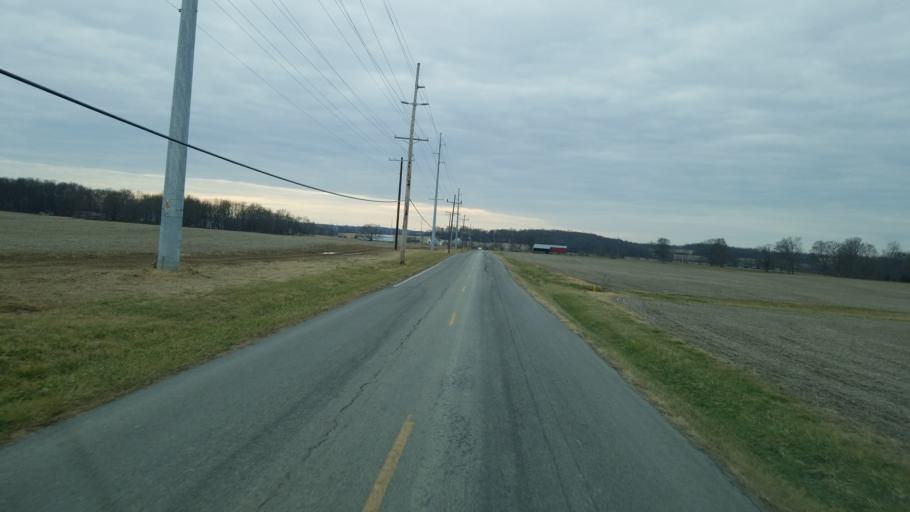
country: US
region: Ohio
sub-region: Highland County
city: Hillsboro
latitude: 39.2354
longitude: -83.5130
